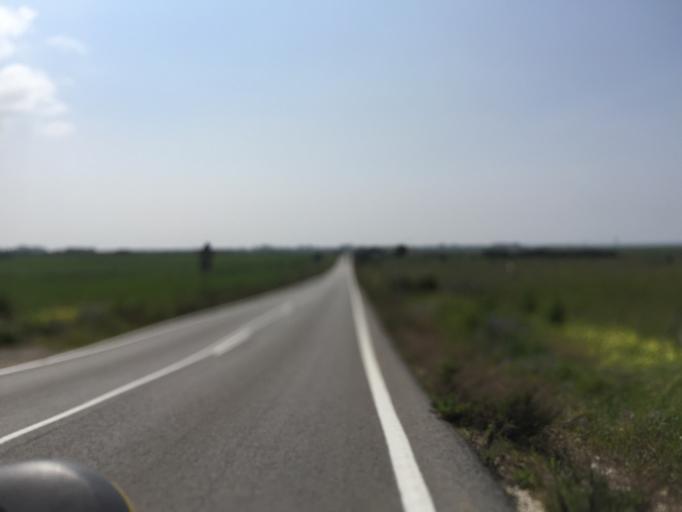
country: ES
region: Andalusia
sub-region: Provincia de Cadiz
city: Conil de la Frontera
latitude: 36.2272
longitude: -6.0397
